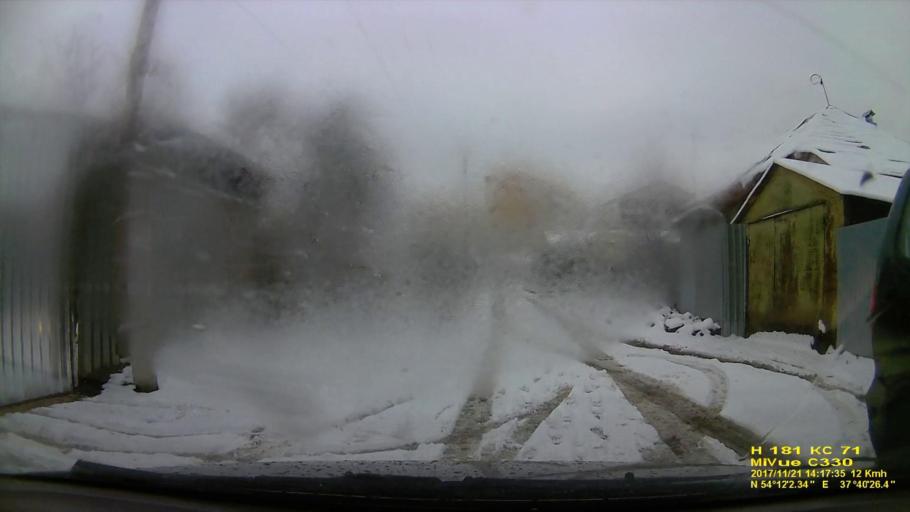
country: RU
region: Tula
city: Tula
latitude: 54.2006
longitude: 37.6740
